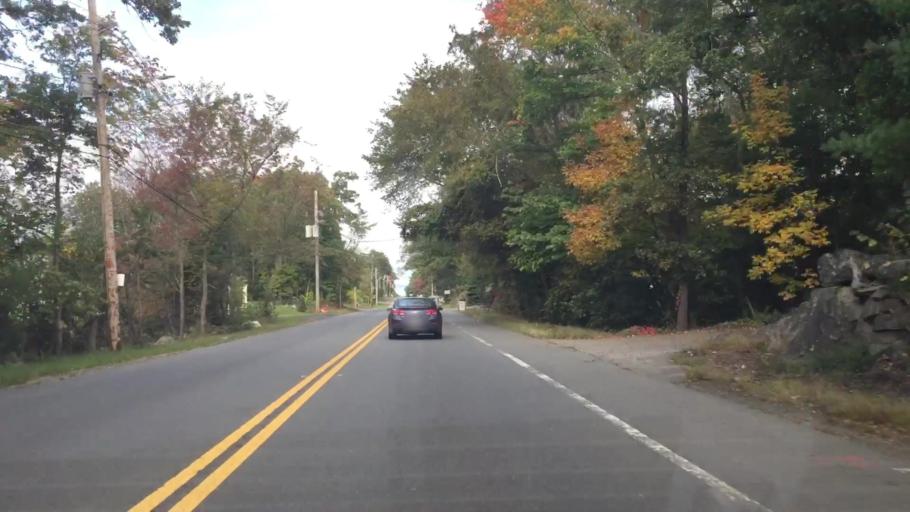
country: US
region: Massachusetts
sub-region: Essex County
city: Middleton
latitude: 42.6216
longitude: -71.0538
